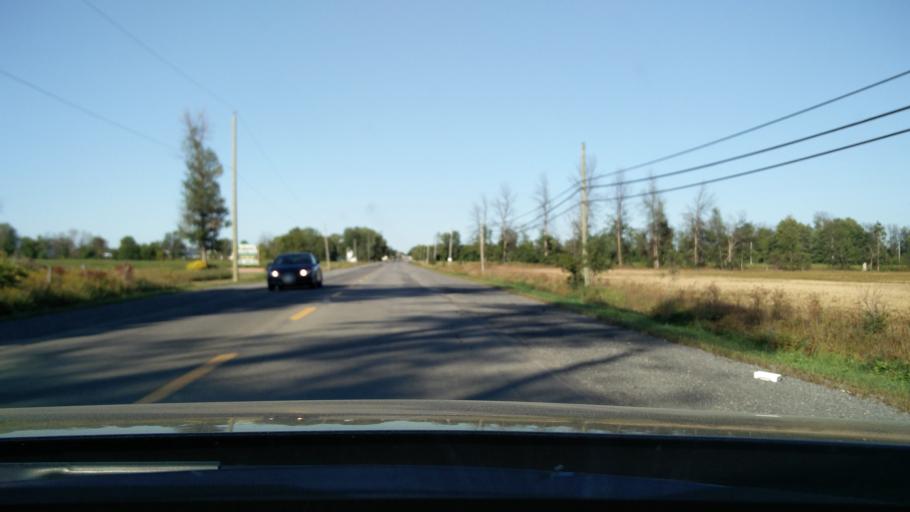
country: CA
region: Ontario
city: Bells Corners
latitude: 45.1834
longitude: -75.8559
